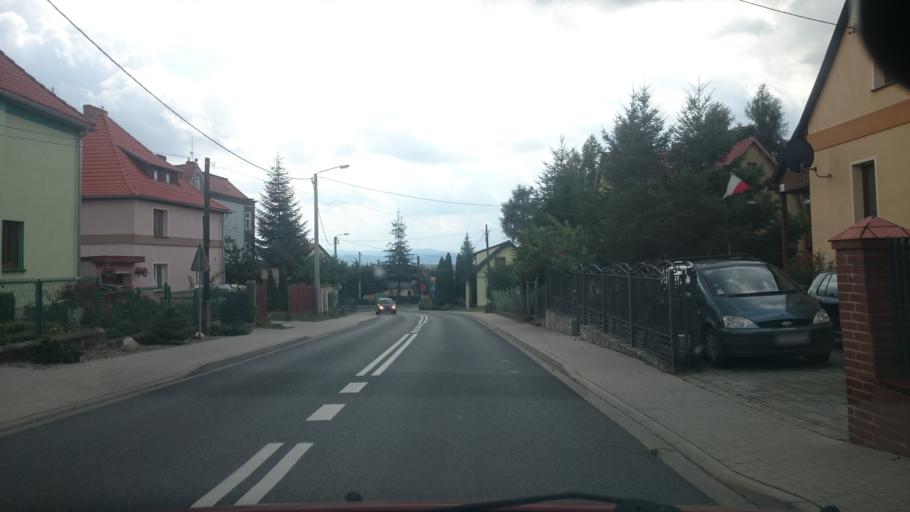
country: PL
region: Lower Silesian Voivodeship
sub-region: Powiat zabkowicki
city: Zabkowice Slaskie
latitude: 50.5891
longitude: 16.8205
